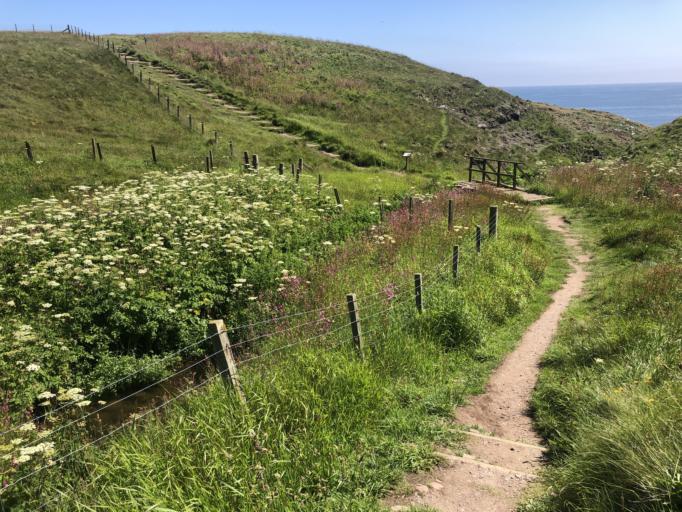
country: GB
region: Scotland
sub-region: Aberdeenshire
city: Stonehaven
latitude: 56.9103
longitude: -2.1987
